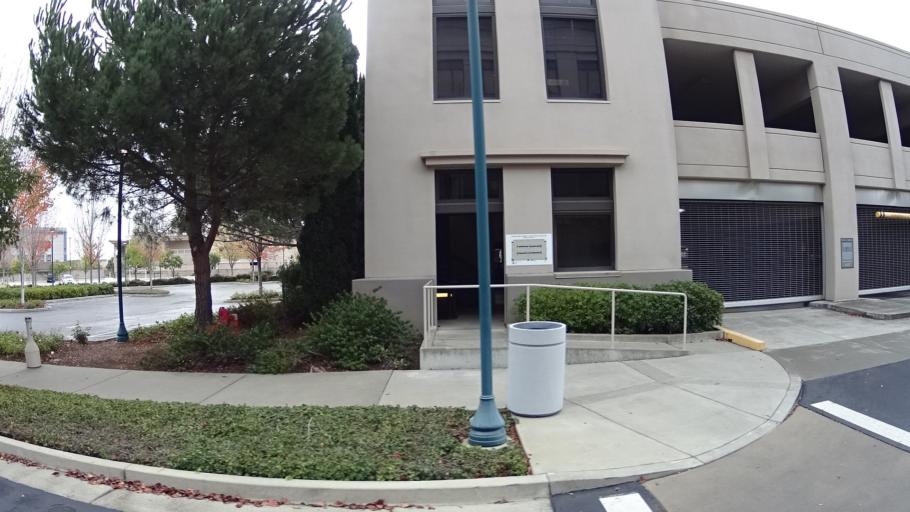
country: US
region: California
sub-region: San Mateo County
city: Foster City
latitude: 37.5428
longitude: -122.2932
